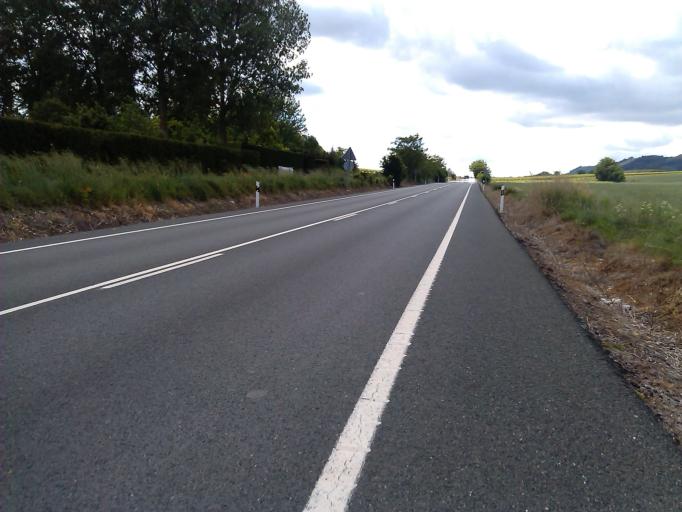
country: ES
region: La Rioja
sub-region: Provincia de La Rioja
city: Hormilla
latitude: 42.4331
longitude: -2.7856
